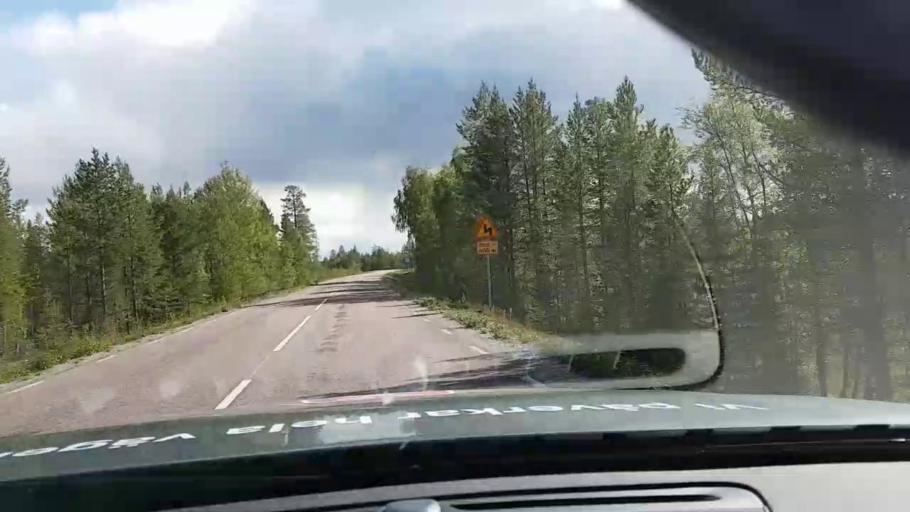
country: SE
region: Vaesterbotten
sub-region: Asele Kommun
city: Asele
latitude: 63.9055
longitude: 17.3434
